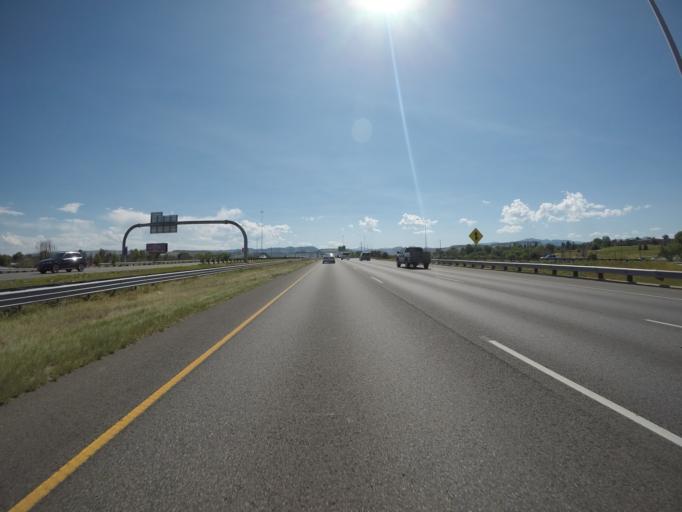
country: US
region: Colorado
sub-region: Jefferson County
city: Applewood
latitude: 39.7807
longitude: -105.1356
